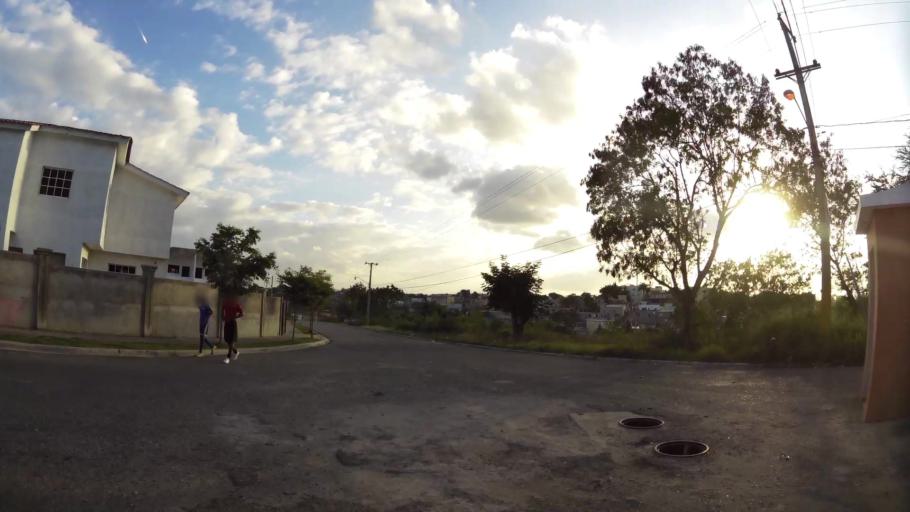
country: DO
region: Nacional
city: La Agustina
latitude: 18.5462
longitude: -69.9219
